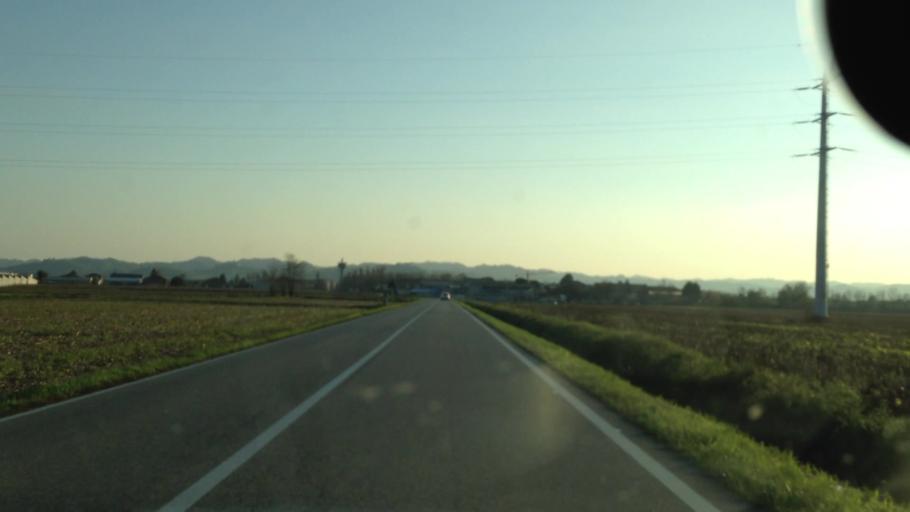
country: IT
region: Piedmont
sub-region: Provincia di Vercelli
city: Crescentino
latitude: 45.2055
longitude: 8.1039
